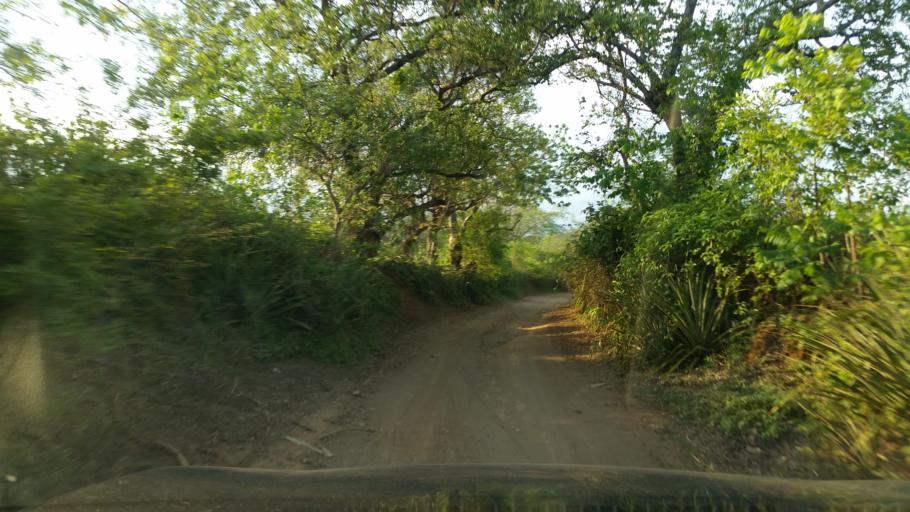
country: NI
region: Managua
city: Masachapa
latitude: 11.7935
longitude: -86.4702
